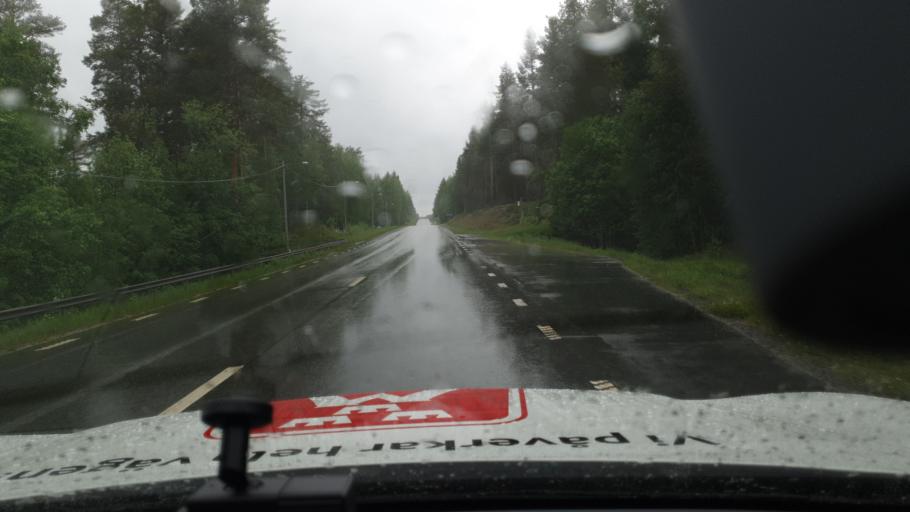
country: SE
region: Vaesterbotten
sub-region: Lycksele Kommun
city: Lycksele
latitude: 64.5363
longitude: 18.7596
